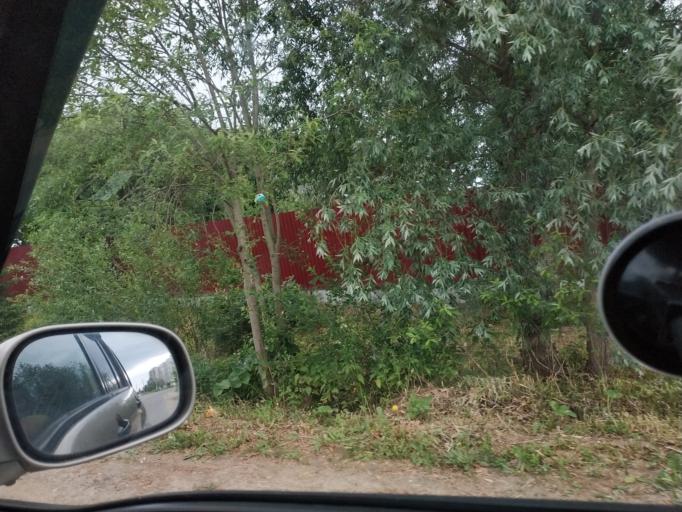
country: RU
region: Moskovskaya
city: Krasnoarmeysk
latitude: 56.0864
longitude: 38.2253
